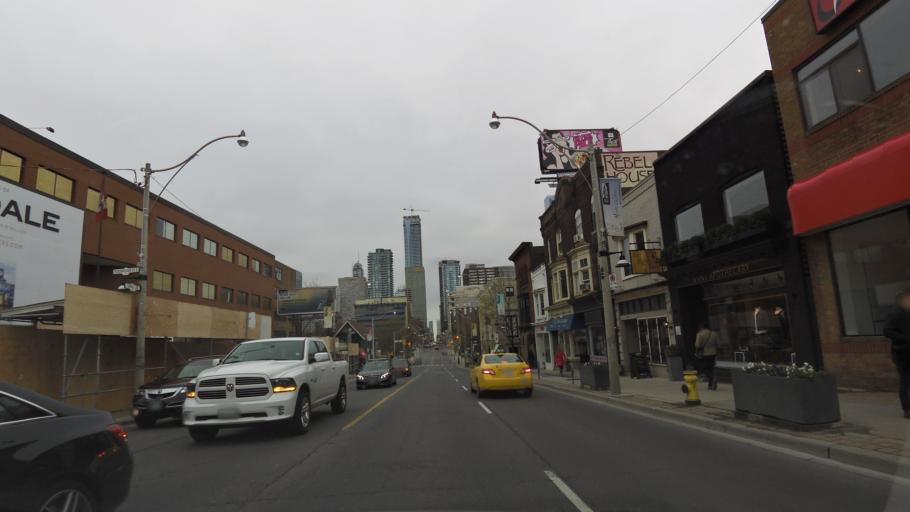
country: CA
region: Ontario
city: Toronto
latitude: 43.6778
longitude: -79.3899
